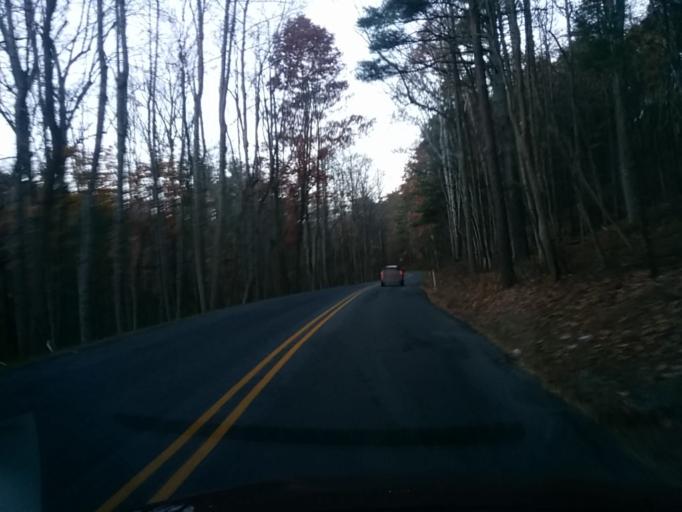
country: US
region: Virginia
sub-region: City of Lexington
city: Lexington
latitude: 37.8902
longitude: -79.5999
